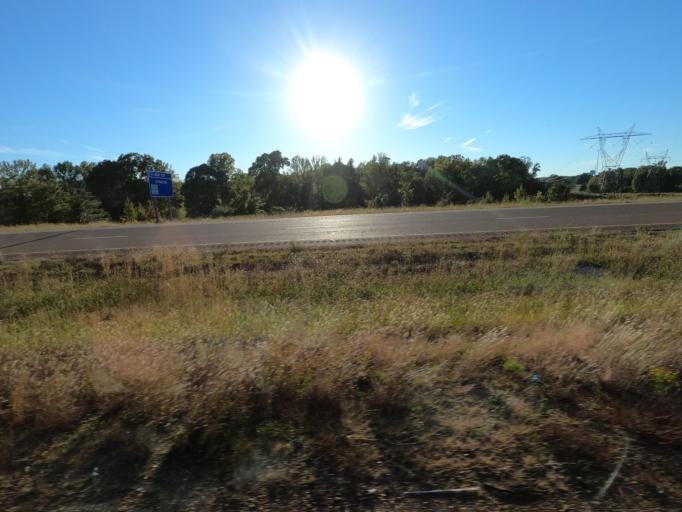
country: US
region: Tennessee
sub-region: Fayette County
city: Hickory Withe
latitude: 35.1783
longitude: -89.6489
